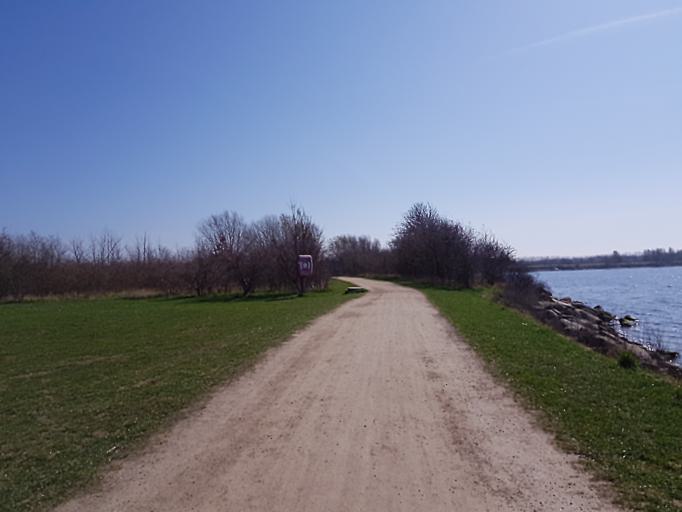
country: DK
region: Capital Region
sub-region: Frederiksberg Kommune
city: Frederiksberg
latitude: 55.6371
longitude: 12.5265
